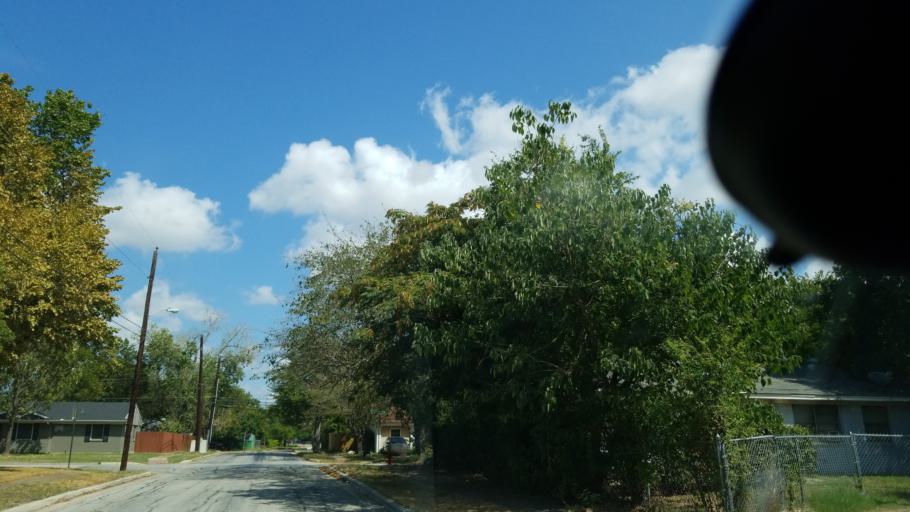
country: US
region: Texas
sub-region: Dallas County
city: Grand Prairie
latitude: 32.7169
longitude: -96.9987
